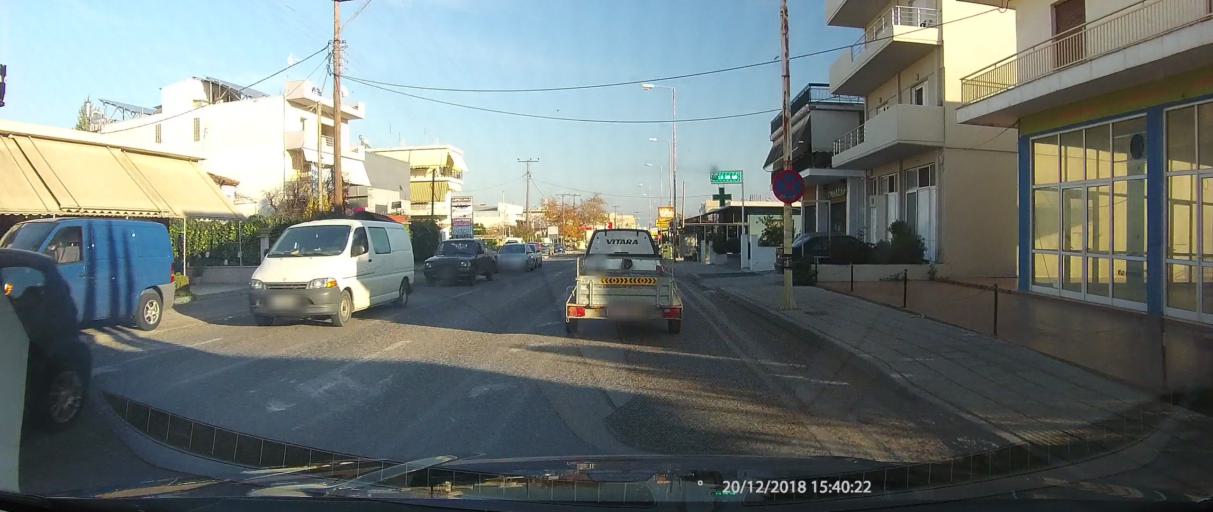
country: GR
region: Central Greece
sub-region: Nomos Fthiotidos
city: Stavros
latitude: 38.8931
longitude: 22.3747
